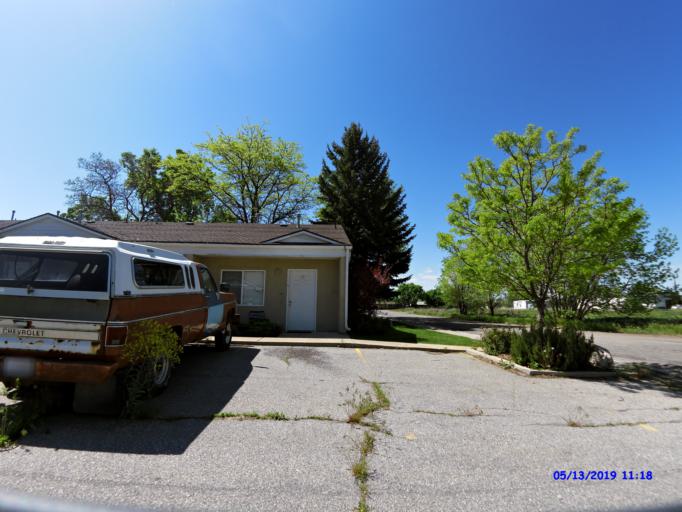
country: US
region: Utah
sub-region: Weber County
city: Harrisville
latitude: 41.2812
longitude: -111.9675
